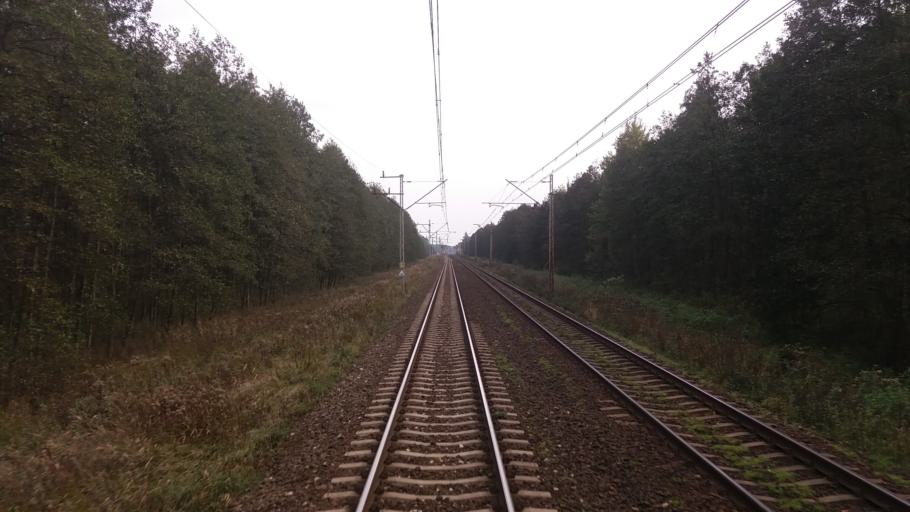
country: PL
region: West Pomeranian Voivodeship
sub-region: Powiat stargardzki
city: Kobylanka
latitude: 53.3740
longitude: 14.8491
